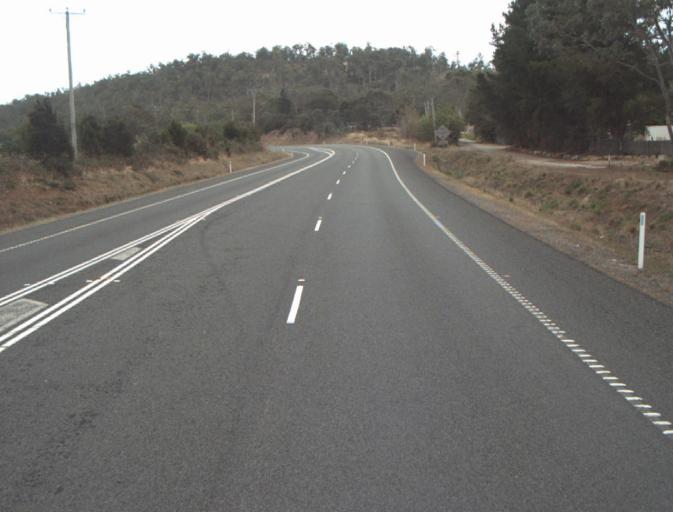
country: AU
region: Tasmania
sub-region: Launceston
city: Mayfield
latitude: -41.2463
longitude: 147.0193
